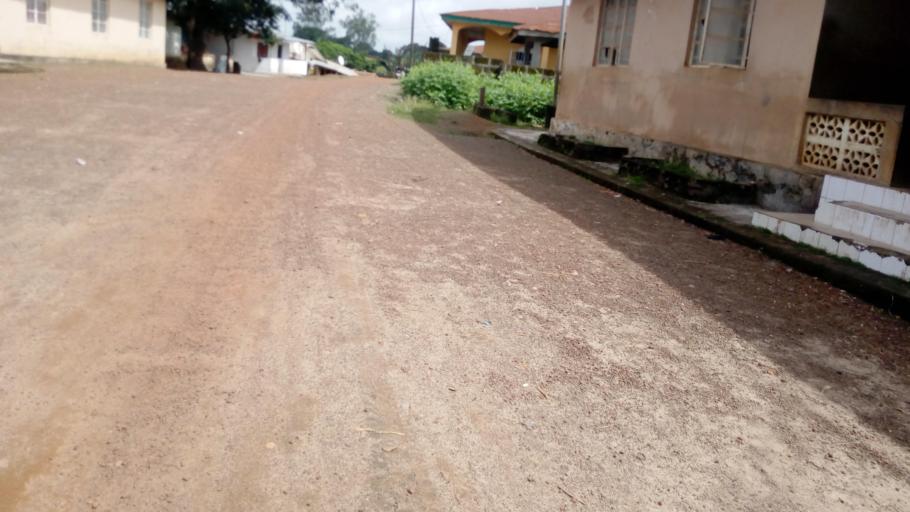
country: SL
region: Northern Province
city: Makeni
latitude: 8.8885
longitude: -12.0331
